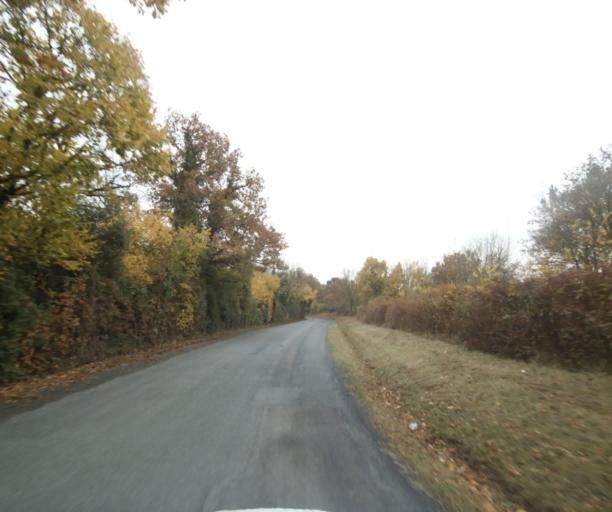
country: FR
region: Poitou-Charentes
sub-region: Departement de la Charente-Maritime
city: Saintes
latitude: 45.7372
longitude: -0.6654
